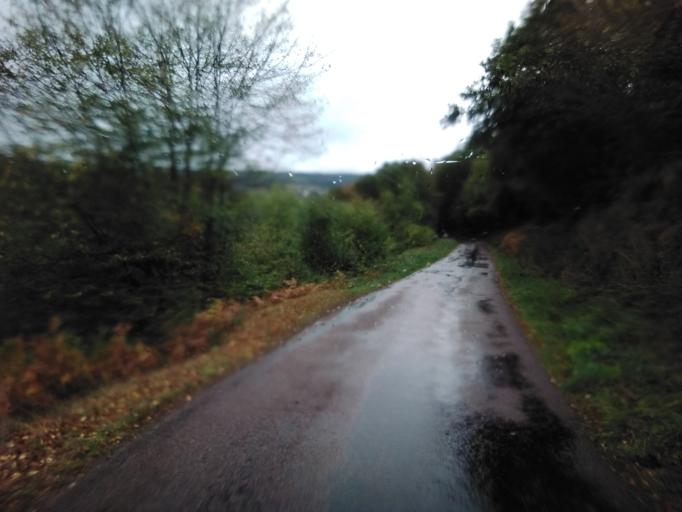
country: FR
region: Bourgogne
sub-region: Departement de la Nievre
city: Lormes
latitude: 47.3383
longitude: 3.9209
